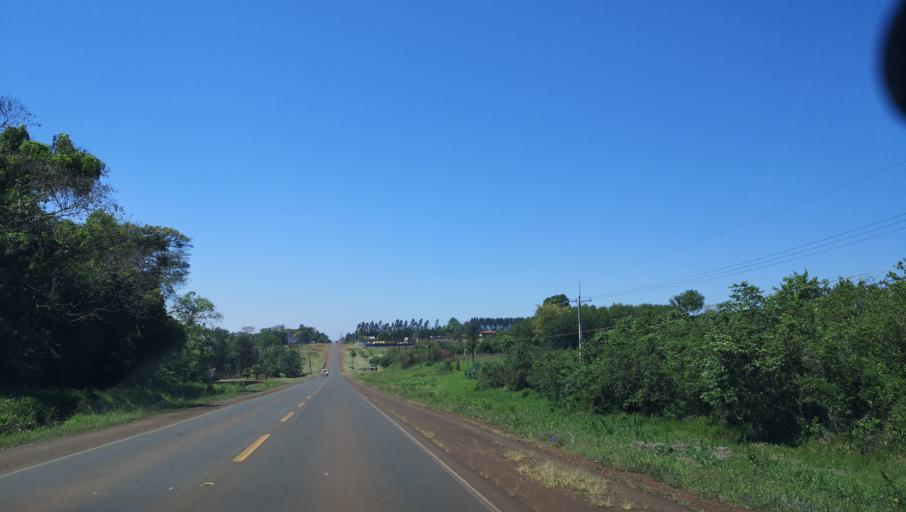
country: PY
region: Itapua
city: San Juan del Parana
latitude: -27.2695
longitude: -55.9565
